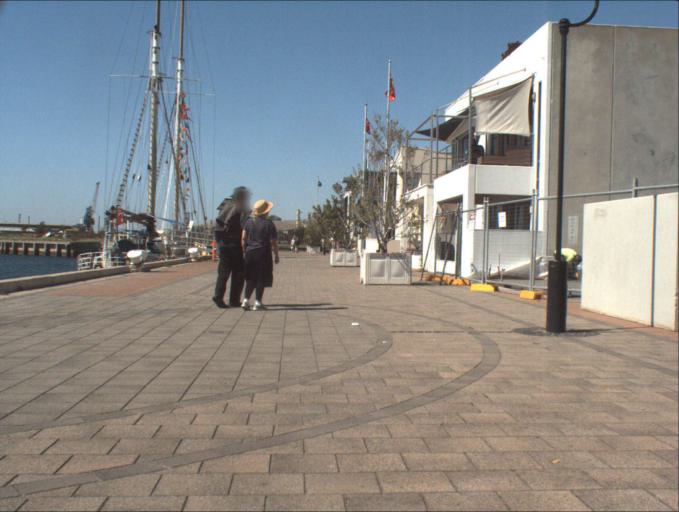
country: AU
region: South Australia
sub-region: Port Adelaide Enfield
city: Birkenhead
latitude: -34.8417
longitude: 138.5058
